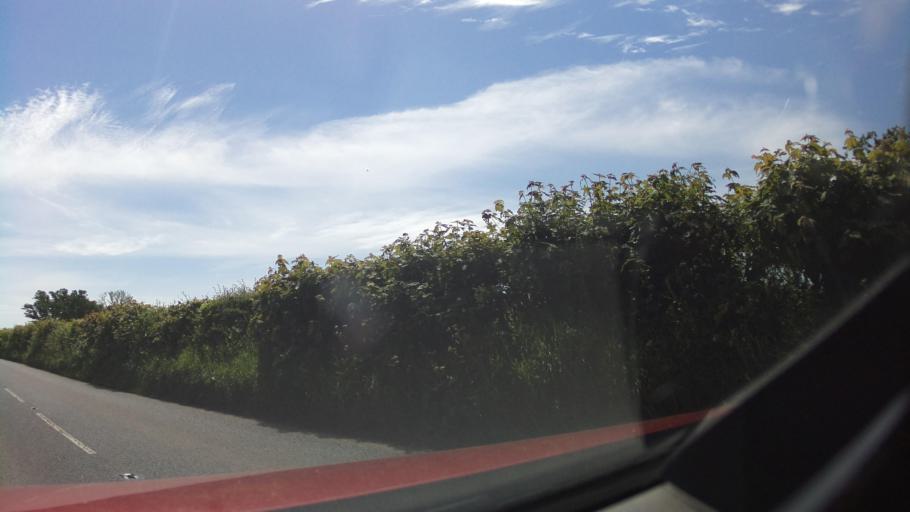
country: GB
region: England
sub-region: Devon
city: Uffculme
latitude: 50.8411
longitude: -3.3147
